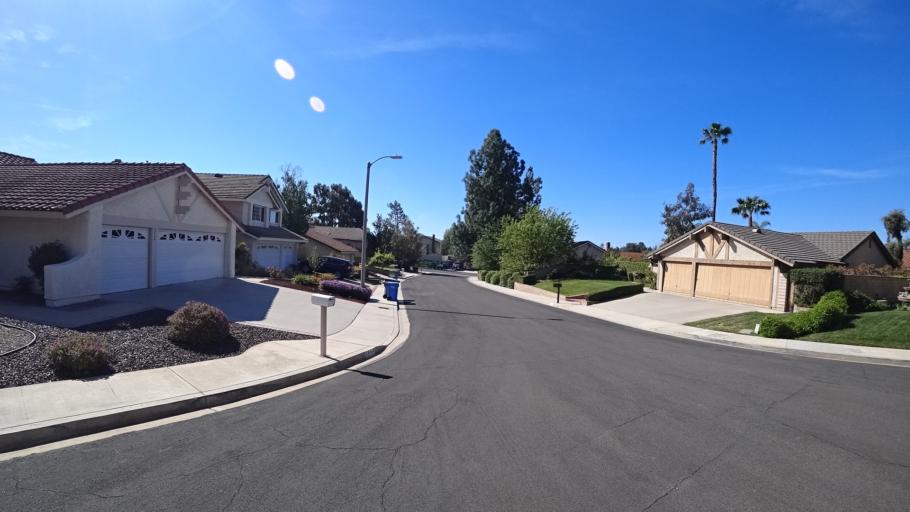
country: US
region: California
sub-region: Ventura County
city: Moorpark
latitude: 34.2298
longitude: -118.8600
